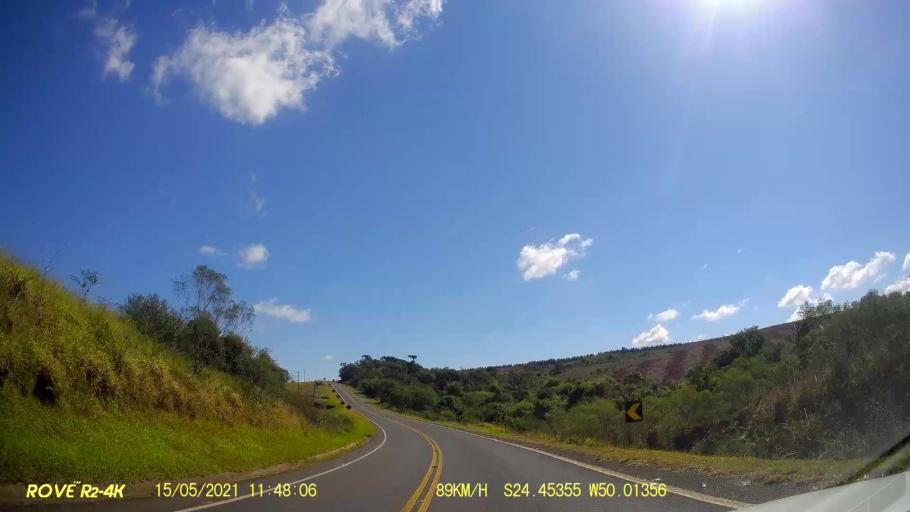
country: BR
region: Parana
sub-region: Pirai Do Sul
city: Pirai do Sul
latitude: -24.4541
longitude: -50.0138
